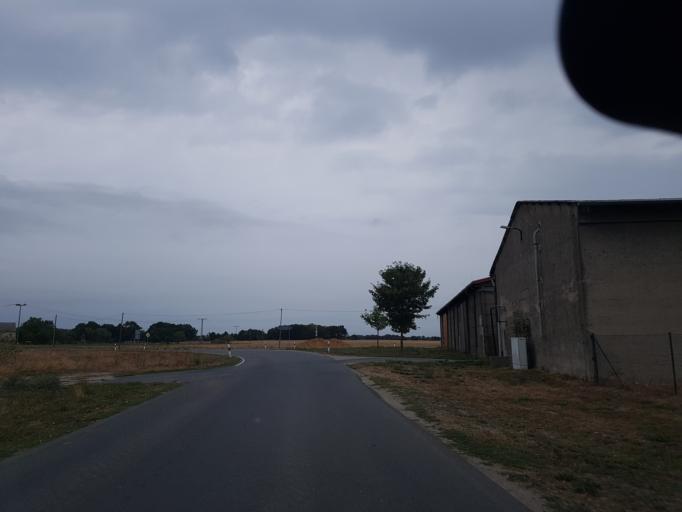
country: DE
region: Saxony-Anhalt
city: Prettin
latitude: 51.7273
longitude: 12.8851
